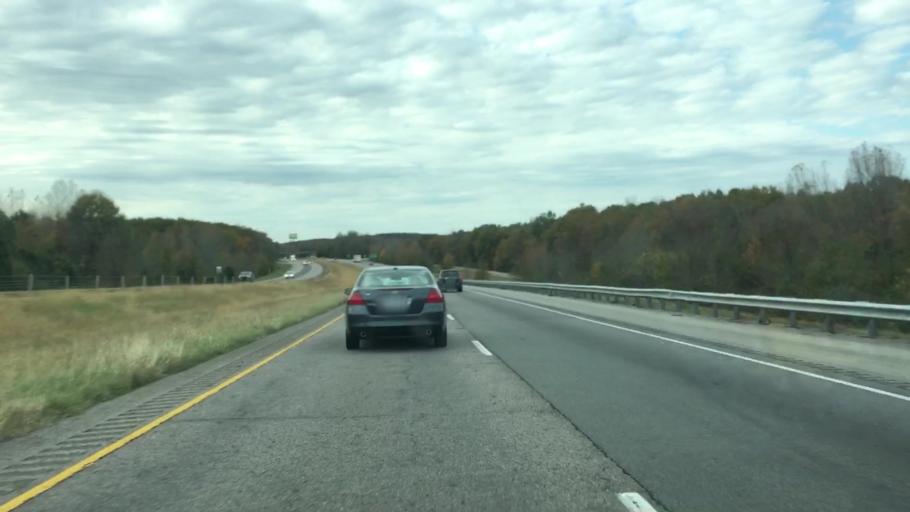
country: US
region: Arkansas
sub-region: Faulkner County
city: Conway
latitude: 35.1497
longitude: -92.5439
